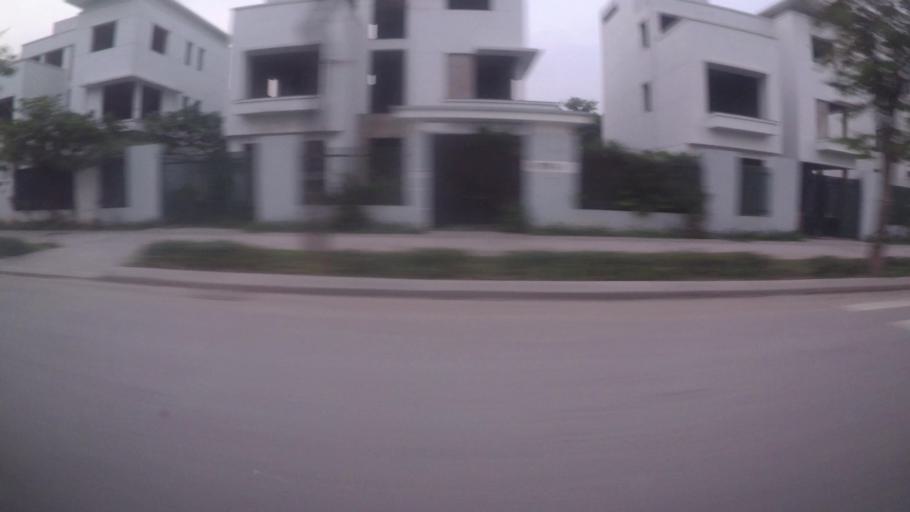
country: VN
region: Ha Noi
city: Tay Ho
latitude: 21.0663
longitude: 105.7932
